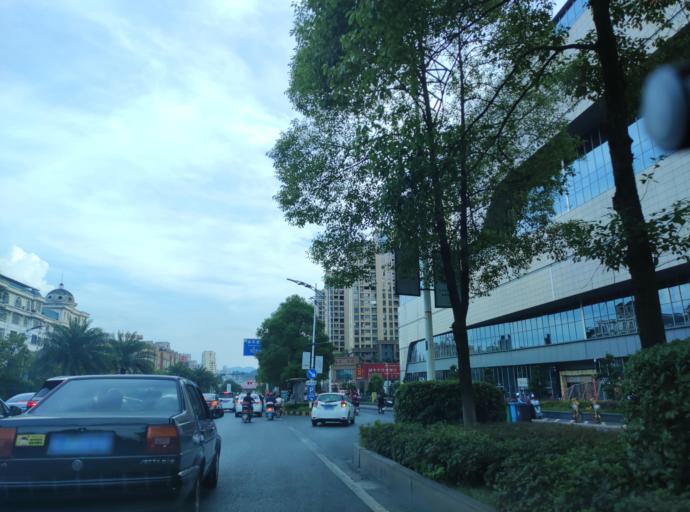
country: CN
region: Jiangxi Sheng
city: Pingxiang
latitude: 27.6347
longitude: 113.8694
